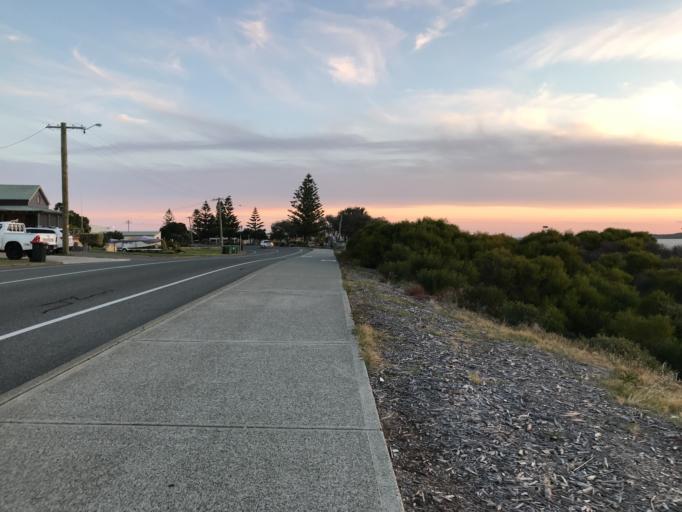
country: AU
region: Western Australia
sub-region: Rockingham
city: Shoalwater
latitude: -32.3027
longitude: 115.7028
